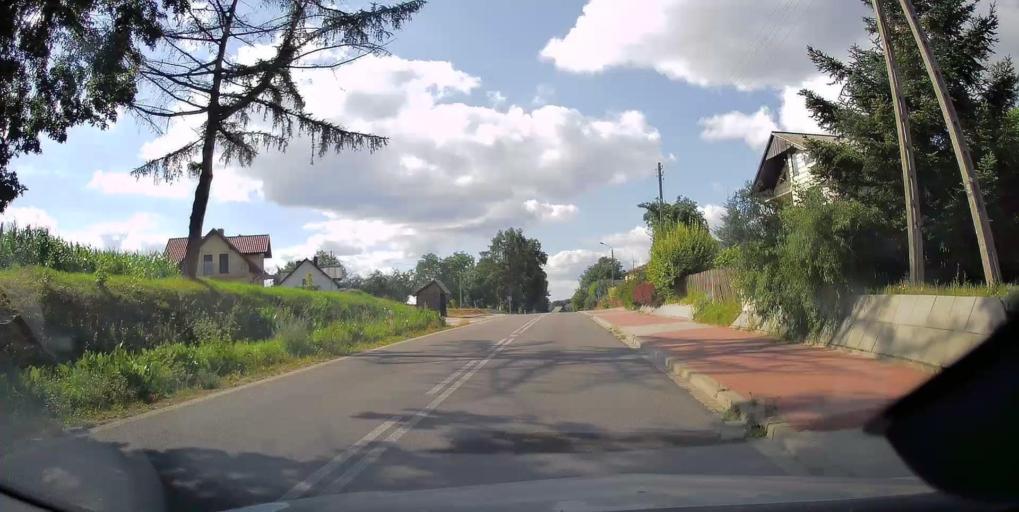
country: PL
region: Swietokrzyskie
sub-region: Powiat kielecki
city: Nowa Slupia
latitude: 50.8745
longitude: 21.0709
